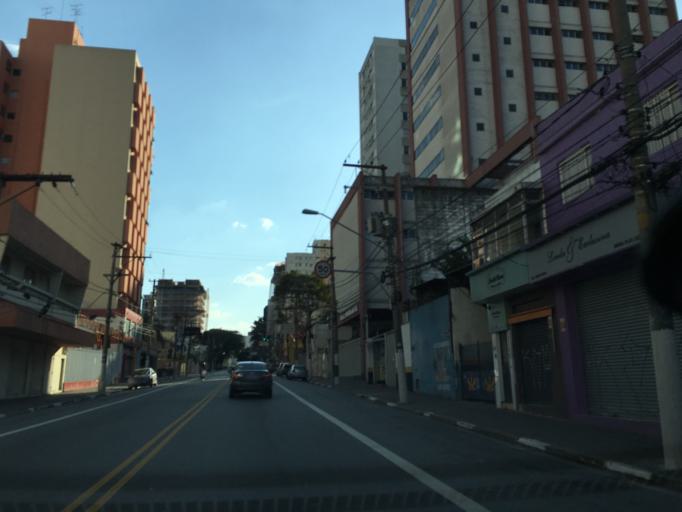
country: BR
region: Sao Paulo
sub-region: Sao Paulo
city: Sao Paulo
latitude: -23.5003
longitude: -46.6276
